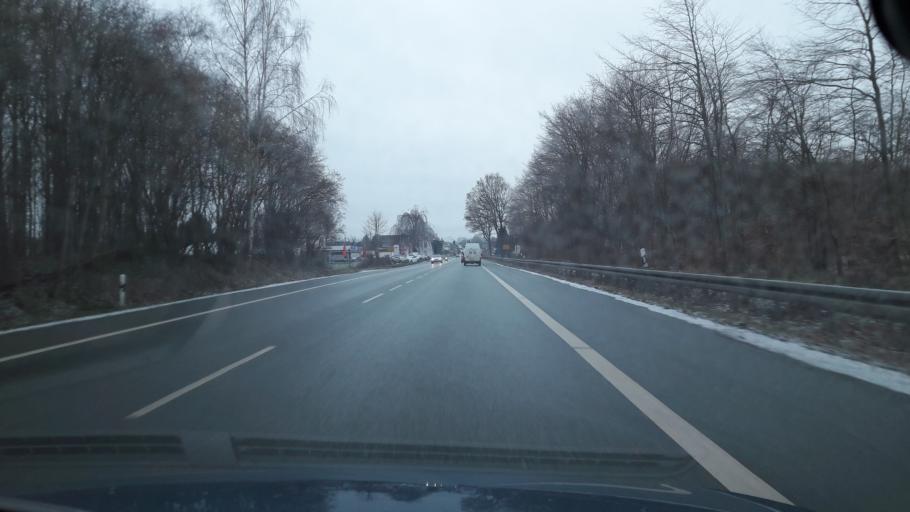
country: DE
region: North Rhine-Westphalia
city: Erwitte
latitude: 51.6206
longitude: 8.3369
